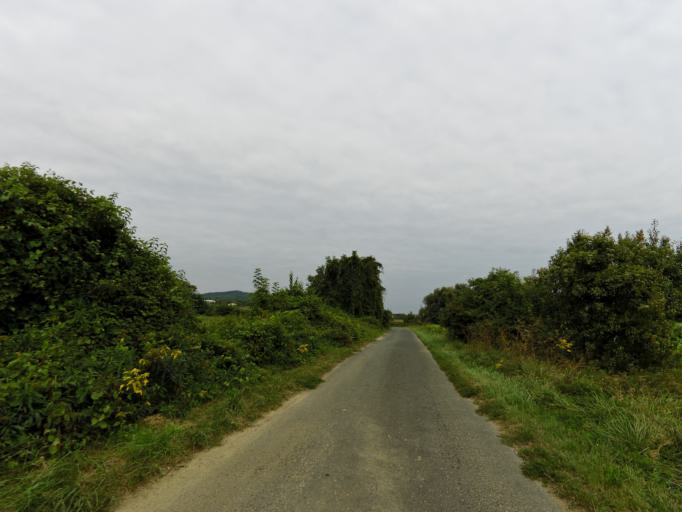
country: HU
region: Veszprem
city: Tapolca
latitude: 46.8435
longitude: 17.3649
